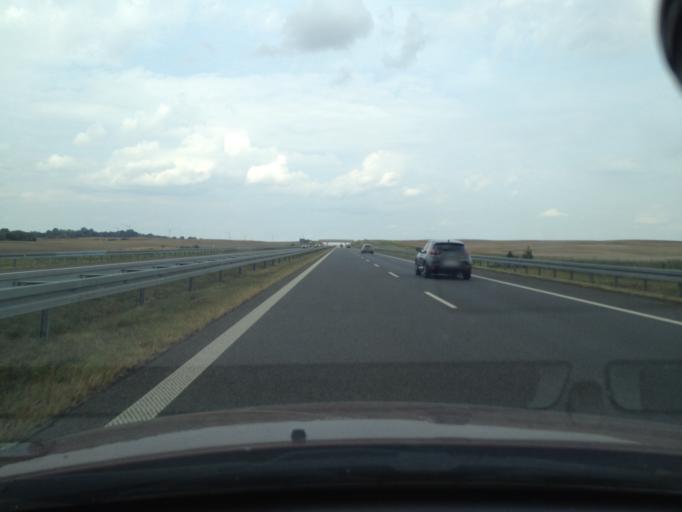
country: PL
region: West Pomeranian Voivodeship
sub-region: Powiat pyrzycki
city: Kozielice
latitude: 53.0585
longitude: 14.8642
